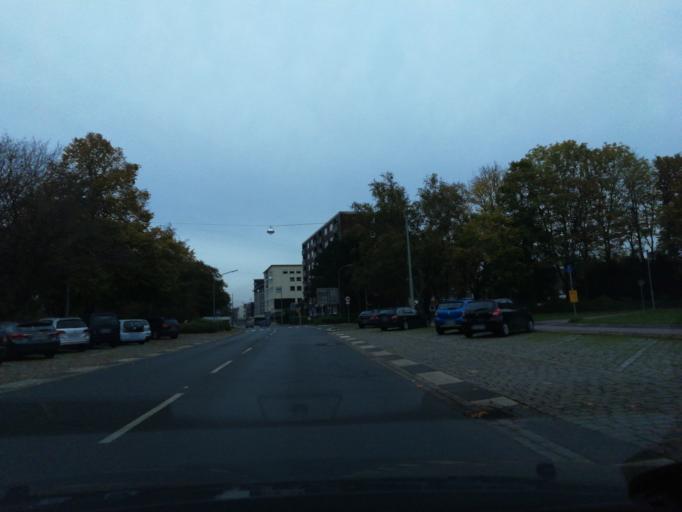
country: DE
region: Lower Saxony
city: Wilhelmshaven
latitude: 53.5243
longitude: 8.1250
